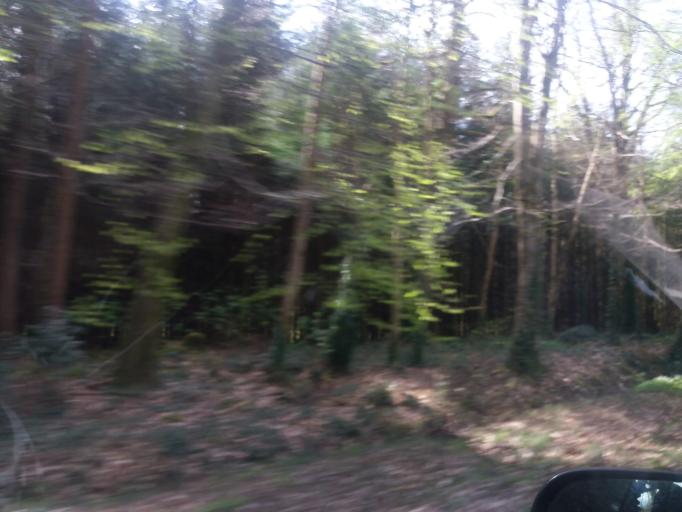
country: GB
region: Northern Ireland
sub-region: Fermanagh District
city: Enniskillen
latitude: 54.3950
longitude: -7.7065
